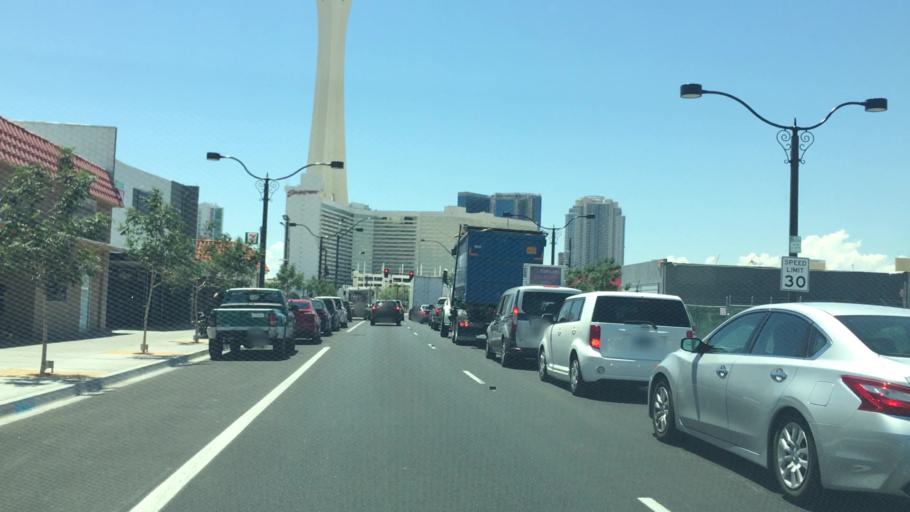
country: US
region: Nevada
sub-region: Clark County
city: Las Vegas
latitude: 36.1533
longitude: -115.1554
